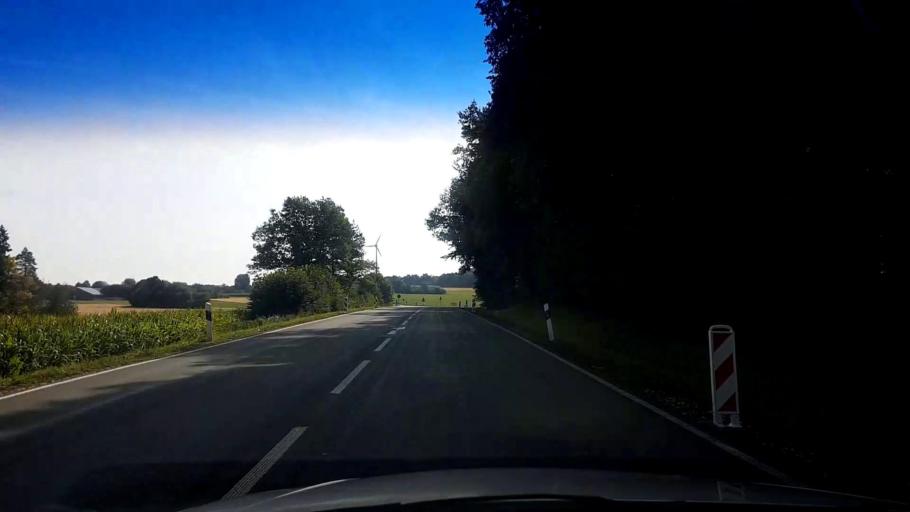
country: DE
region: Bavaria
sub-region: Upper Franconia
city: Hollfeld
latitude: 49.9477
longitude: 11.3234
